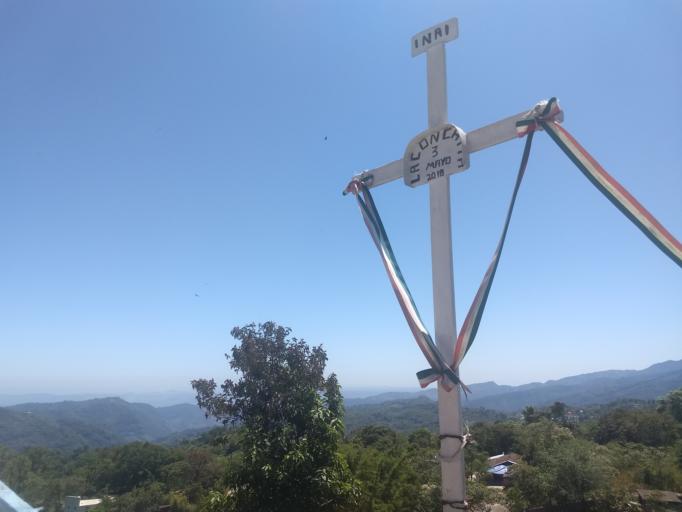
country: MX
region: Puebla
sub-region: Cuetzalan del Progreso
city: Ciudad de Cuetzalan
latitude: 20.0154
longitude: -97.5199
